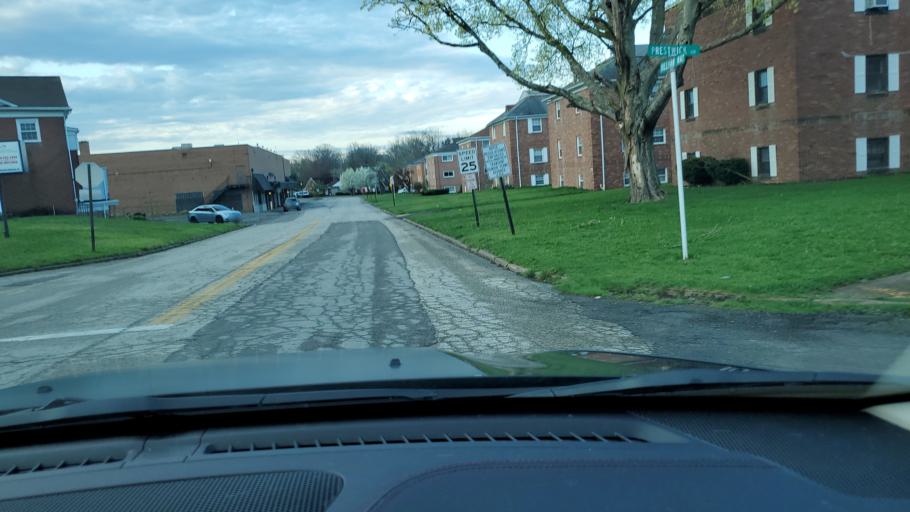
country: US
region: Ohio
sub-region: Mahoning County
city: Boardman
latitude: 41.0600
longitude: -80.6640
